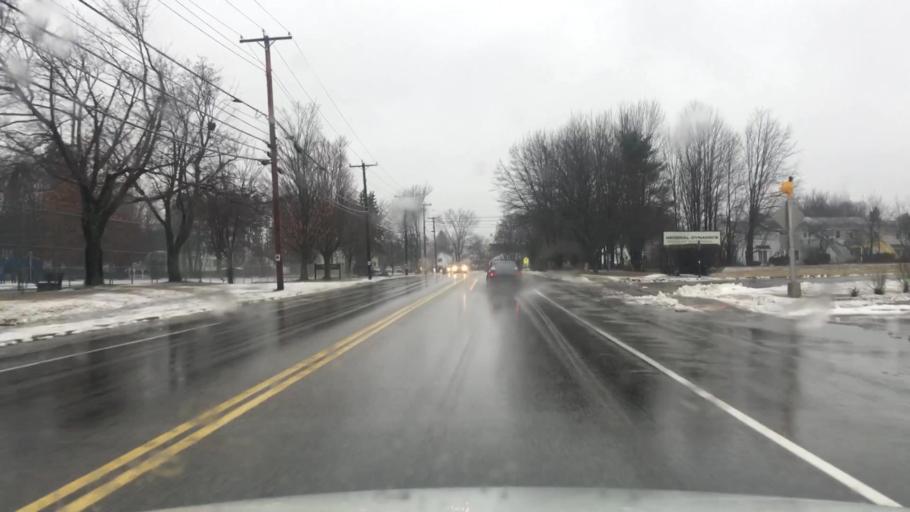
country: US
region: Maine
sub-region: York County
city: Saco
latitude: 43.5128
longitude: -70.4508
